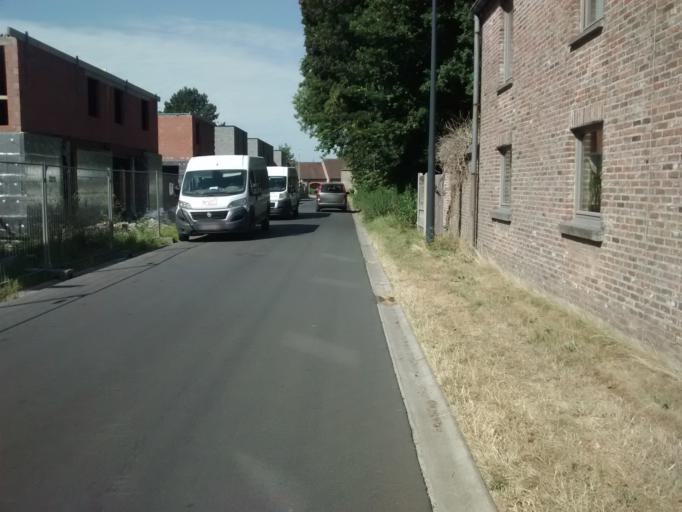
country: BE
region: Flanders
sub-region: Provincie Oost-Vlaanderen
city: Destelbergen
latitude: 51.0713
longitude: 3.7995
